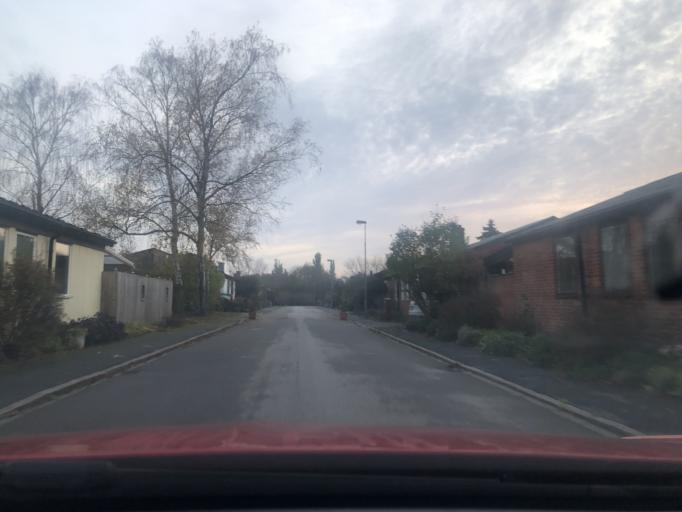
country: SE
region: Skane
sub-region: Burlovs Kommun
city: Arloev
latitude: 55.6010
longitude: 13.0755
